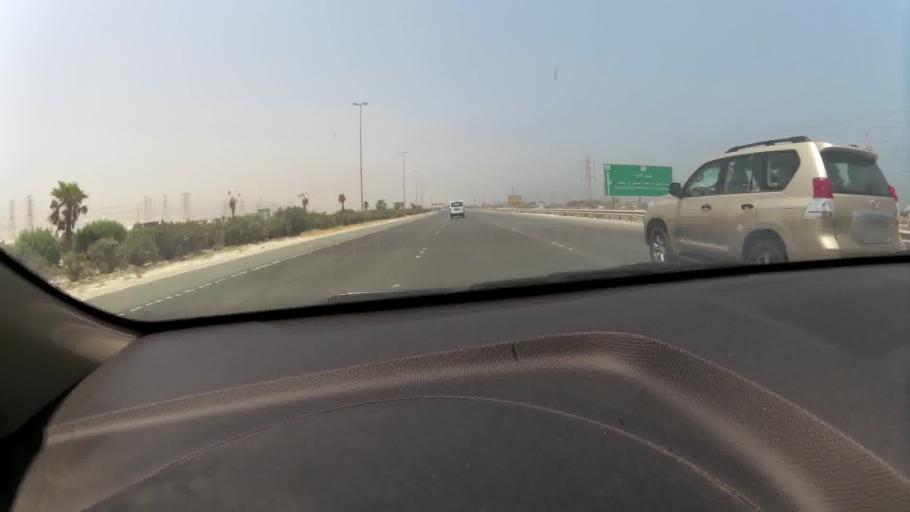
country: KW
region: Al Ahmadi
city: Al Fahahil
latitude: 28.9058
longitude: 48.2164
